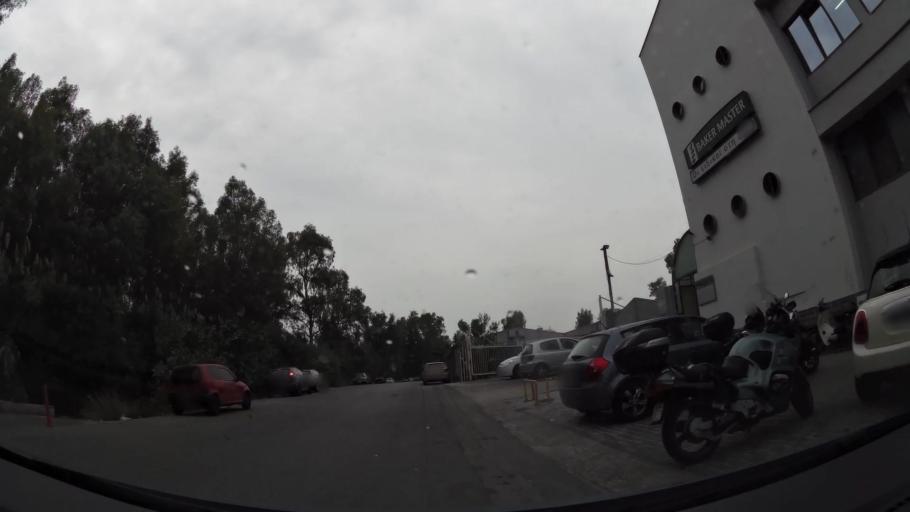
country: GR
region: Attica
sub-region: Nomarchia Athinas
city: Argyroupoli
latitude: 37.9175
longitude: 23.7395
